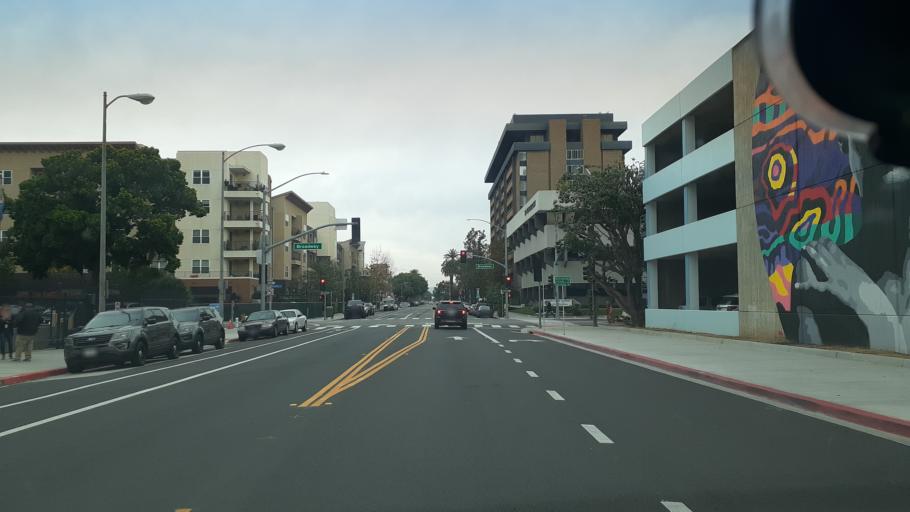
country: US
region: California
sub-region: Los Angeles County
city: Long Beach
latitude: 33.7687
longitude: -118.1963
